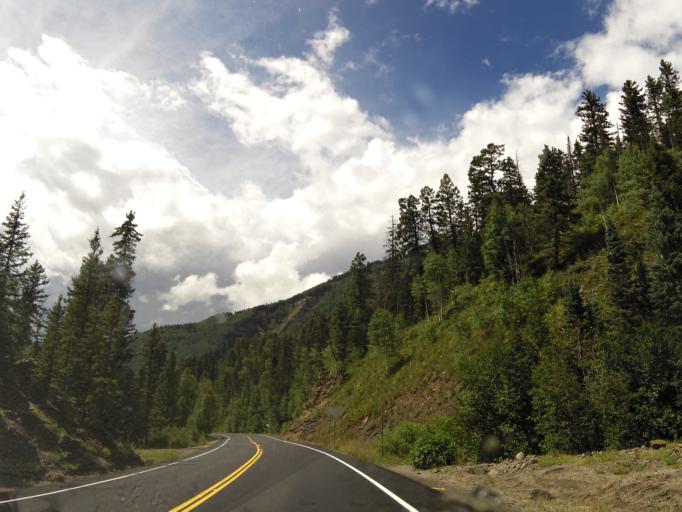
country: US
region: Colorado
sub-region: San Juan County
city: Silverton
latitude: 37.6806
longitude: -107.7865
